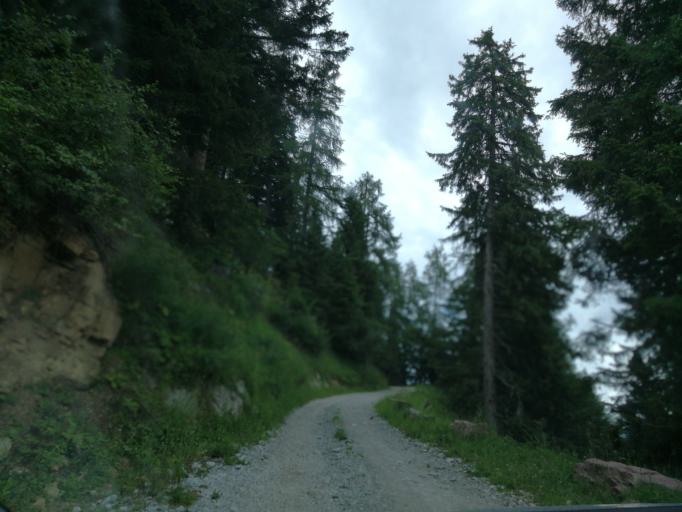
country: IT
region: Trentino-Alto Adige
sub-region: Provincia di Trento
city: Castel Condino
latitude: 45.9388
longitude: 10.5791
